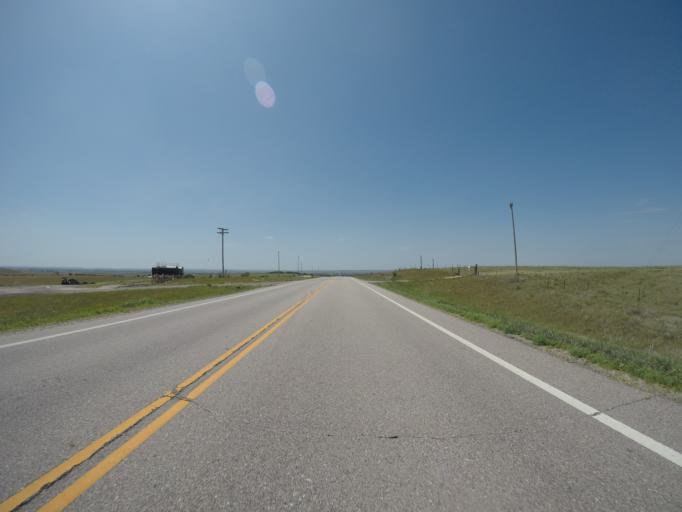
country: US
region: Kansas
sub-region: Osborne County
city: Osborne
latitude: 39.4766
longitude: -98.6943
